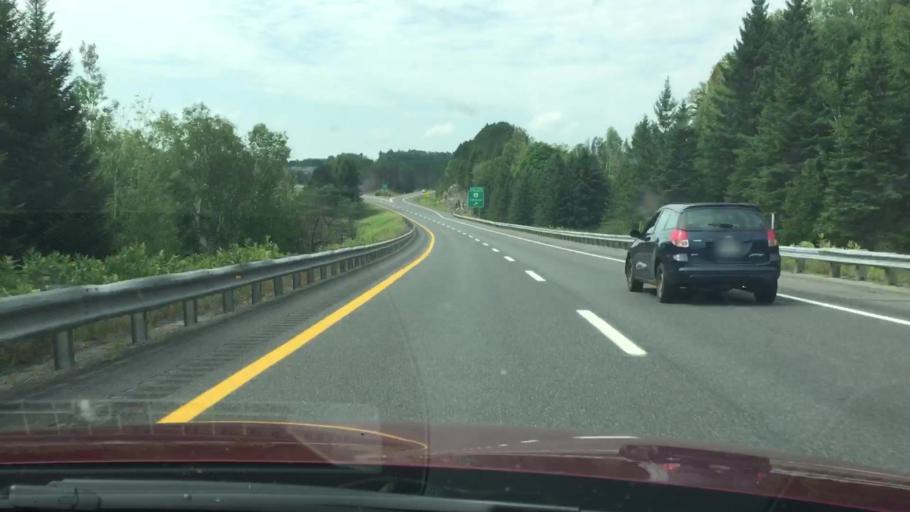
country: US
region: Maine
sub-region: Aroostook County
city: Hodgdon
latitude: 46.1454
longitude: -68.0530
